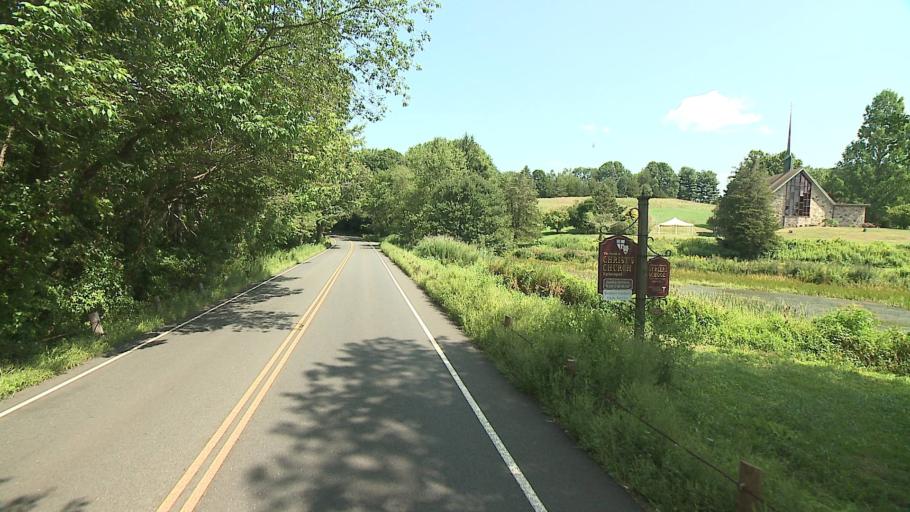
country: US
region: Connecticut
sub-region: Fairfield County
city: Trumbull
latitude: 41.2750
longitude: -73.2948
